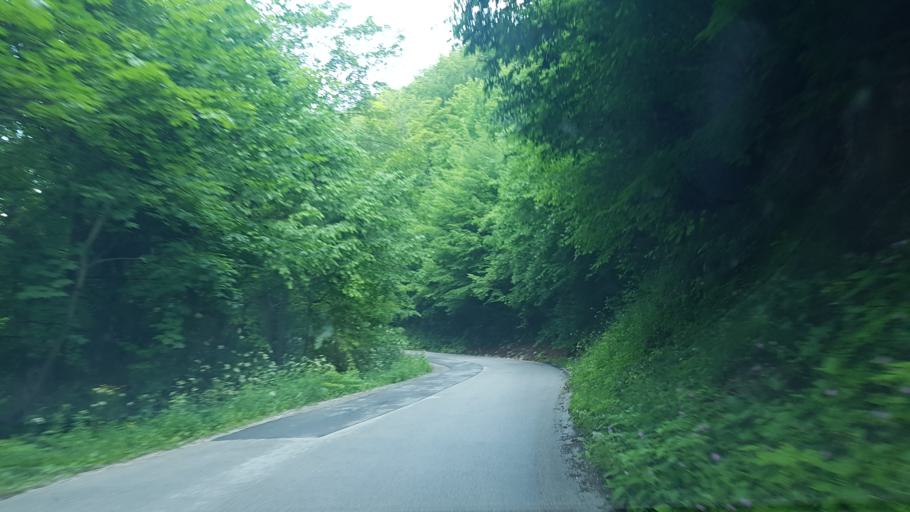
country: SI
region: Dobrna
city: Dobrna
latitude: 46.3867
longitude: 15.1794
